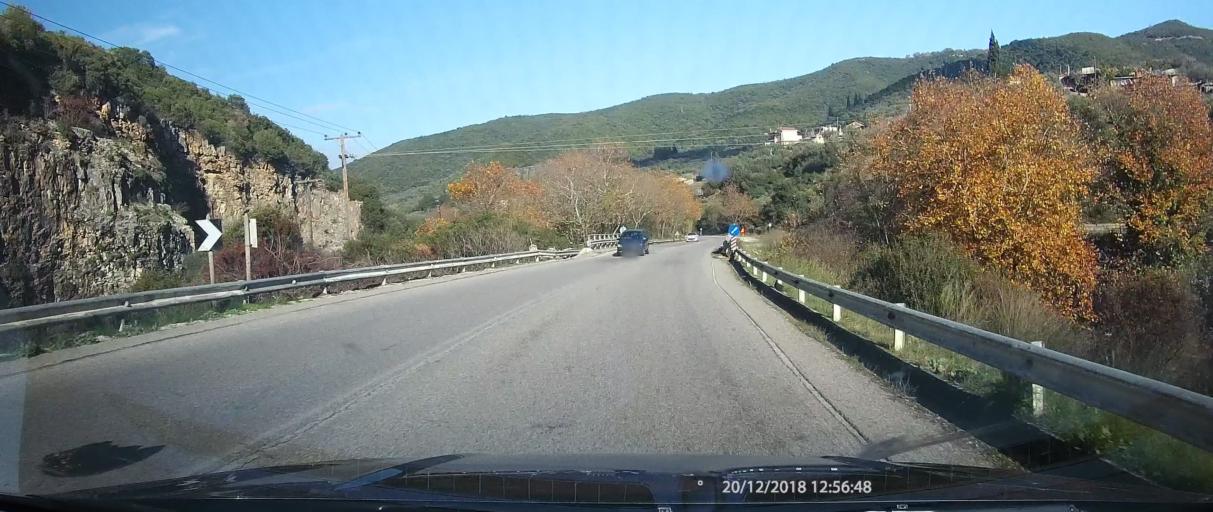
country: GR
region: West Greece
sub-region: Nomos Aitolias kai Akarnanias
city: Pappadhatai
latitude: 38.5151
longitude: 21.3798
